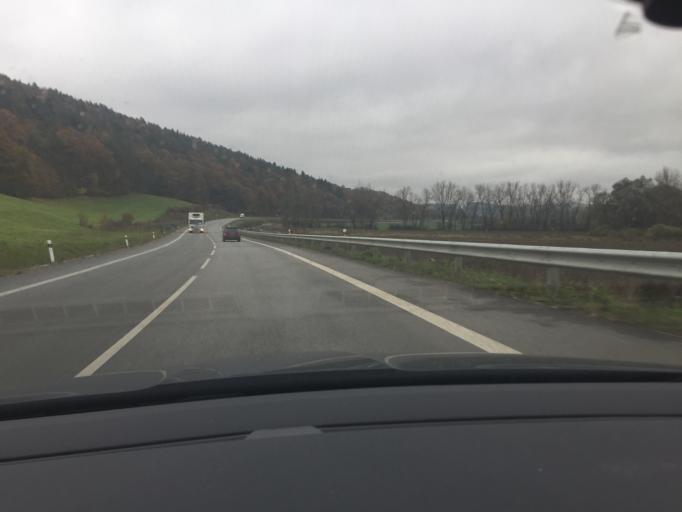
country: SK
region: Presovsky
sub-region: Okres Bardejov
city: Bardejov
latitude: 49.3057
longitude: 21.2232
